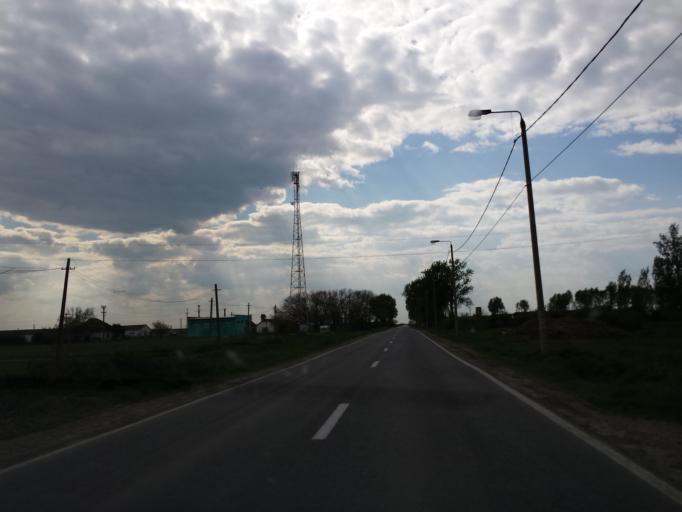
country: RO
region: Timis
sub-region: Comuna Cenad
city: Cenad
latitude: 46.1291
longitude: 20.5571
